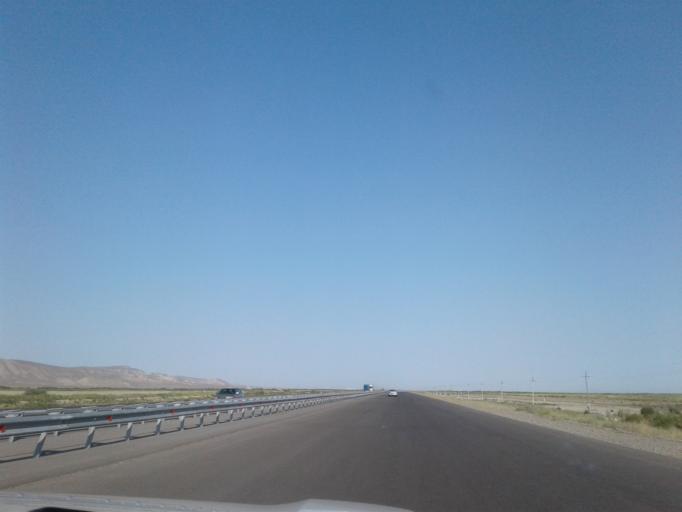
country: TM
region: Balkan
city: Serdar
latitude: 38.9170
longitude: 56.4777
